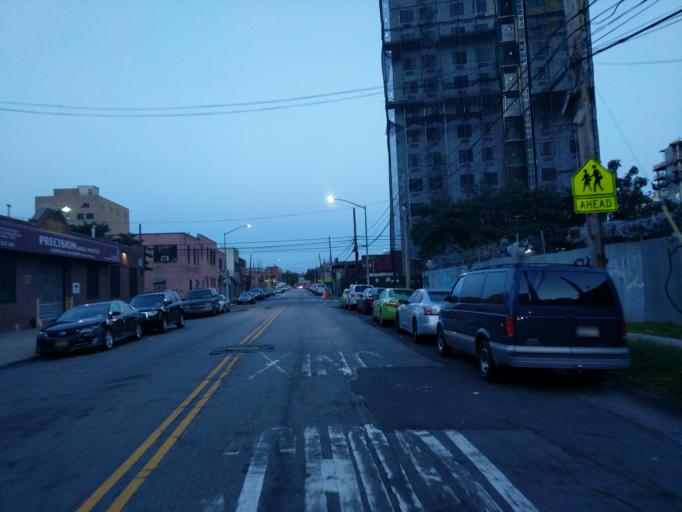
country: US
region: New York
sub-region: Queens County
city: Long Island City
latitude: 40.7592
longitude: -73.9439
